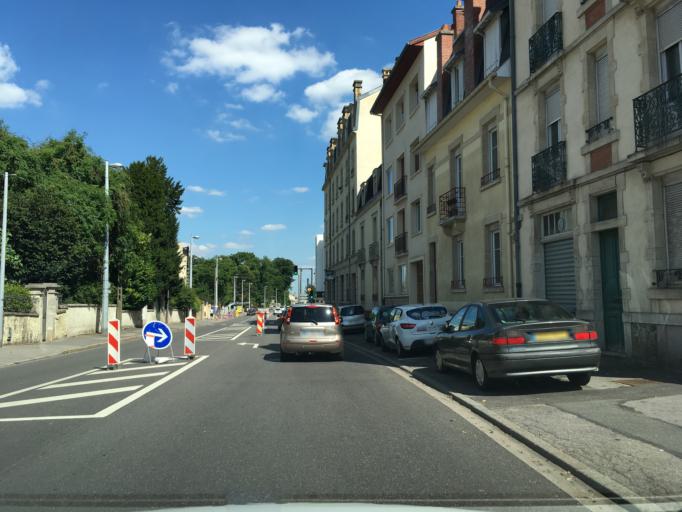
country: FR
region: Lorraine
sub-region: Departement de Meurthe-et-Moselle
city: Laxou
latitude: 48.6971
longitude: 6.1569
